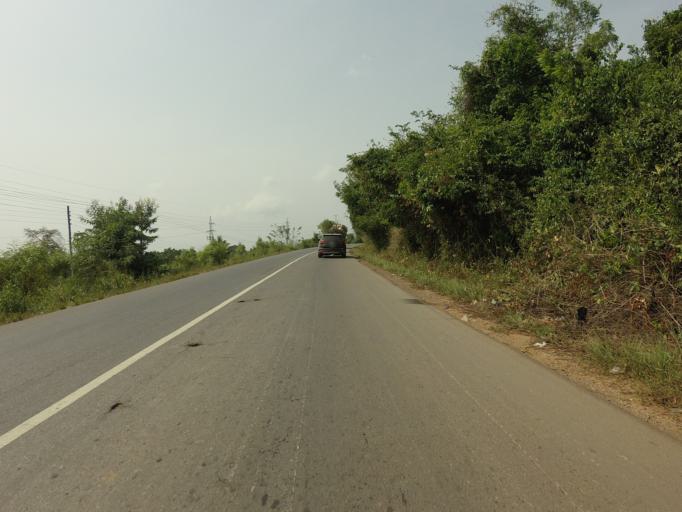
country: GH
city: Akropong
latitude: 6.2377
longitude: 0.1025
